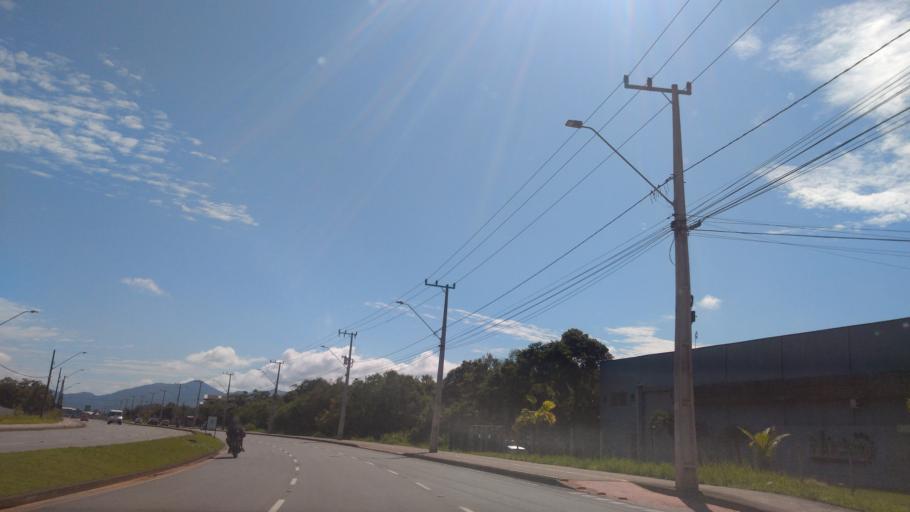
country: BR
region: Santa Catarina
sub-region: Joinville
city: Joinville
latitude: -26.2325
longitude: -48.8087
